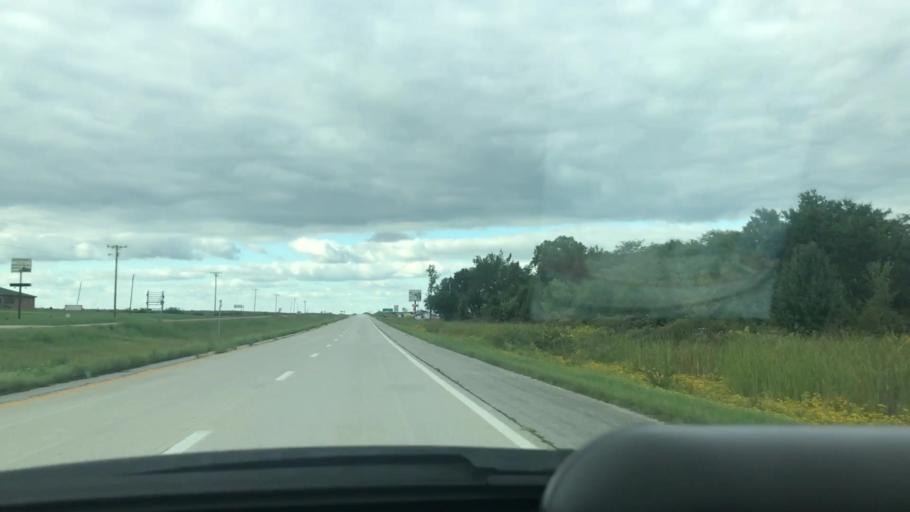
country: US
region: Missouri
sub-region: Benton County
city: Lincoln
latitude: 38.3491
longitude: -93.3399
